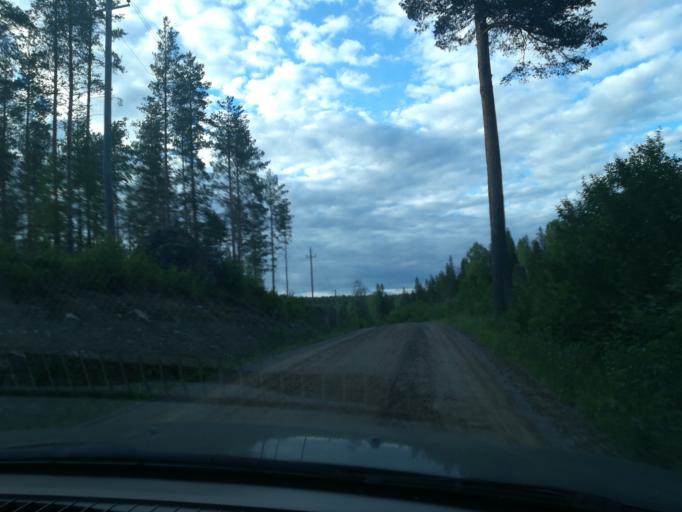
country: FI
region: Southern Savonia
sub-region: Mikkeli
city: Puumala
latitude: 61.5946
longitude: 28.1506
